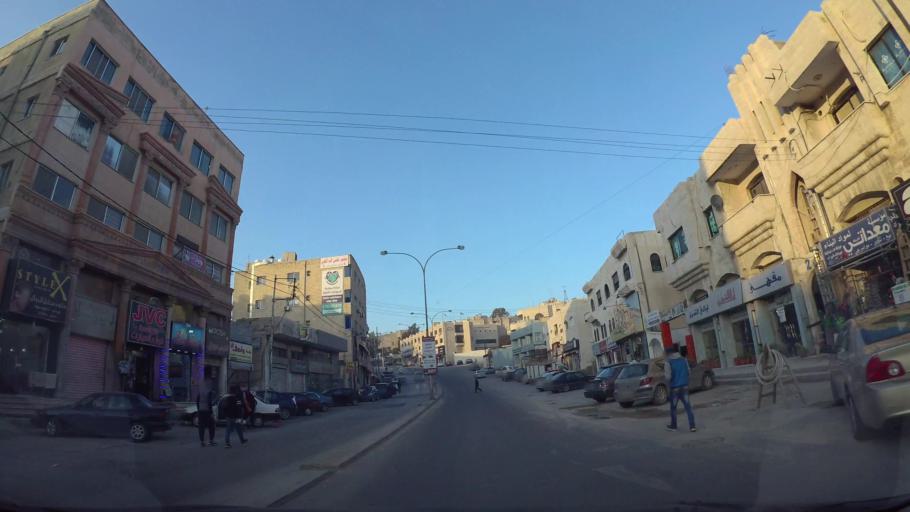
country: JO
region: Amman
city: Amman
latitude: 31.9937
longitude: 35.9456
